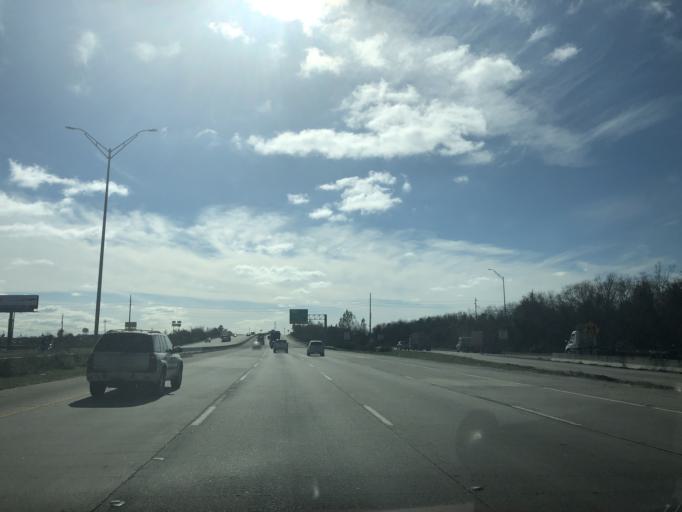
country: US
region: Texas
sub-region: Harris County
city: La Porte
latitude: 29.6787
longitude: -95.0303
